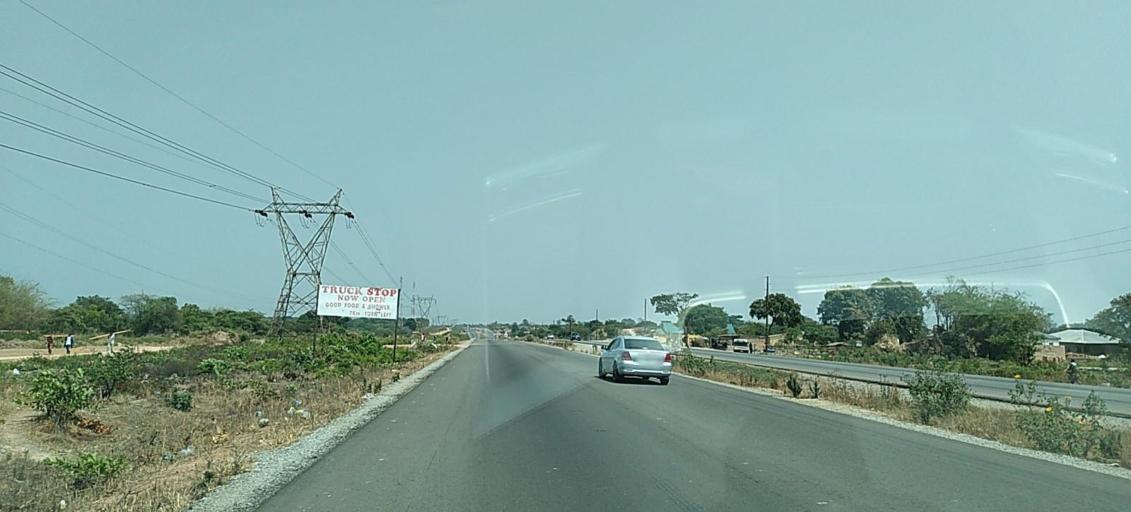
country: ZM
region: Copperbelt
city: Chambishi
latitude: -12.6013
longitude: 27.9657
